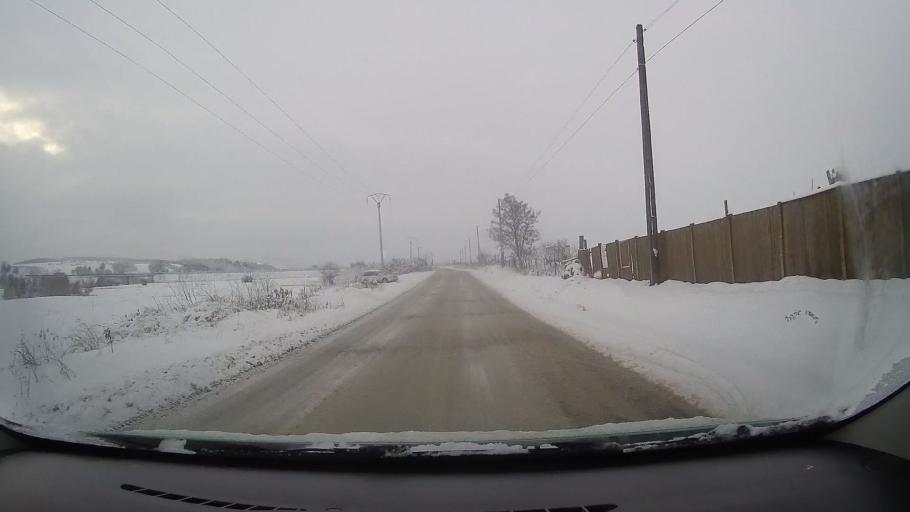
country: RO
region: Alba
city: Vurpar
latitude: 45.9729
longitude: 23.4809
